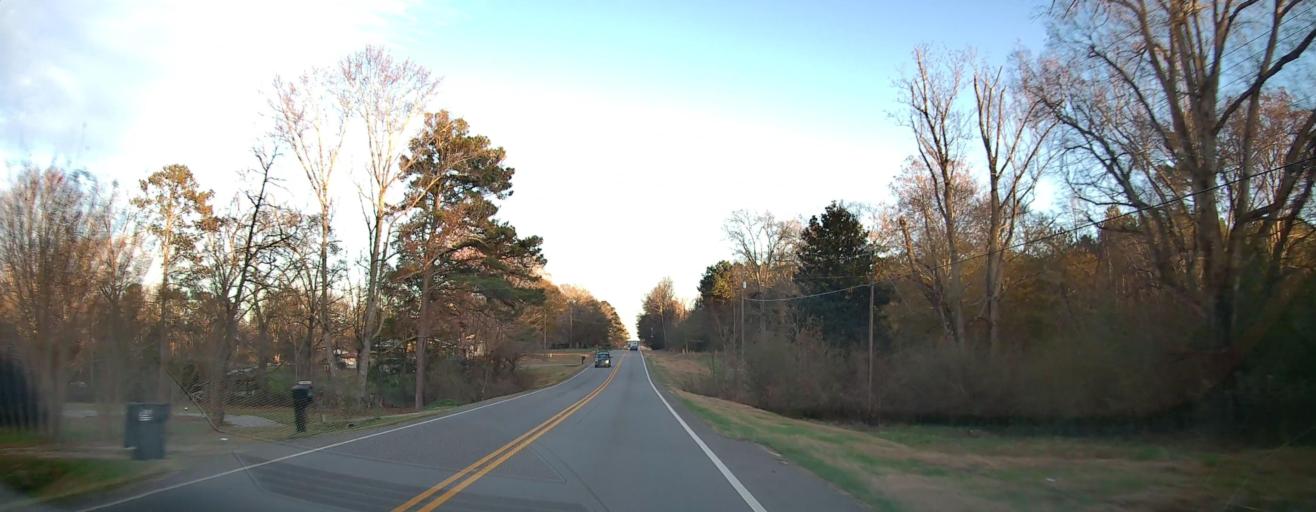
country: US
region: Alabama
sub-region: Etowah County
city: Attalla
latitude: 34.0531
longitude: -86.1953
